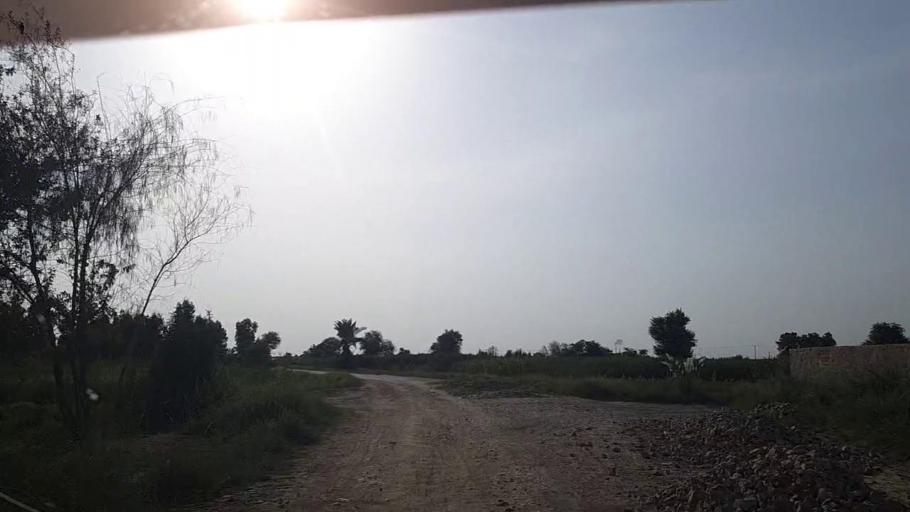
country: PK
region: Sindh
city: Ghotki
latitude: 28.0166
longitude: 69.2924
